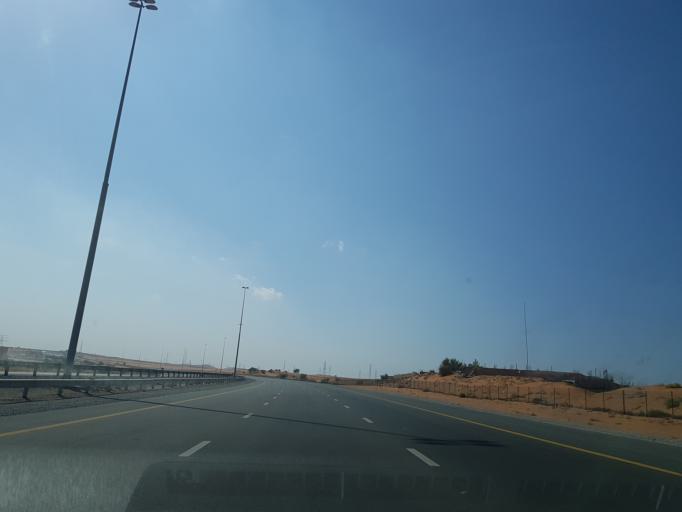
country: AE
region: Ra's al Khaymah
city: Ras al-Khaimah
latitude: 25.7062
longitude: 55.9428
